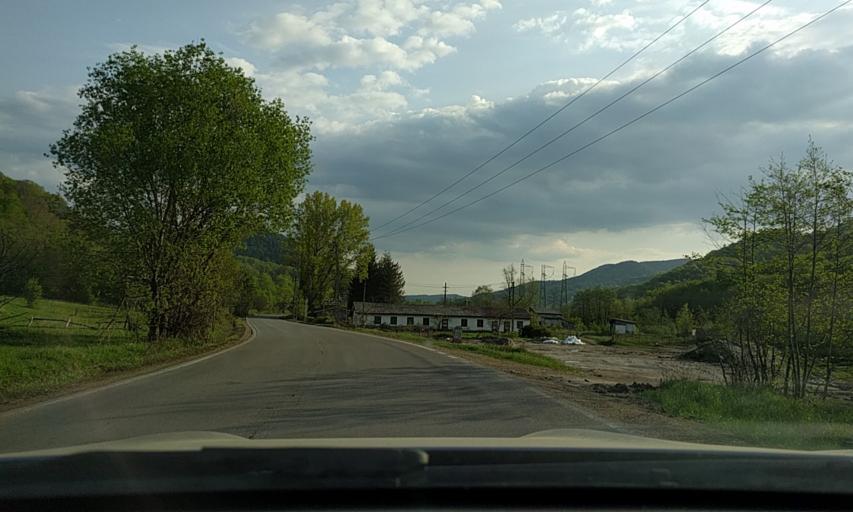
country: RO
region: Bacau
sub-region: Oras Slanic-Moldova
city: Slanic-Moldova
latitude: 46.1286
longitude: 26.4413
